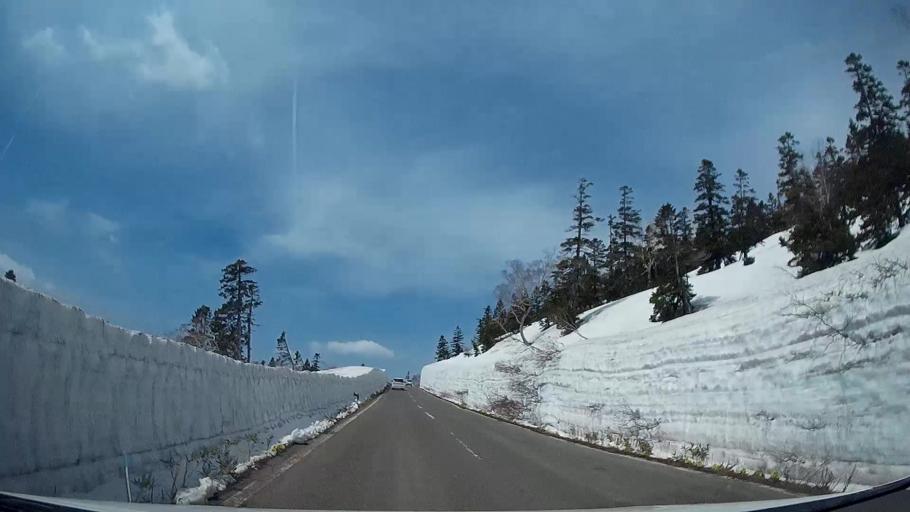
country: JP
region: Akita
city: Hanawa
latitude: 39.9510
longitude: 140.8773
